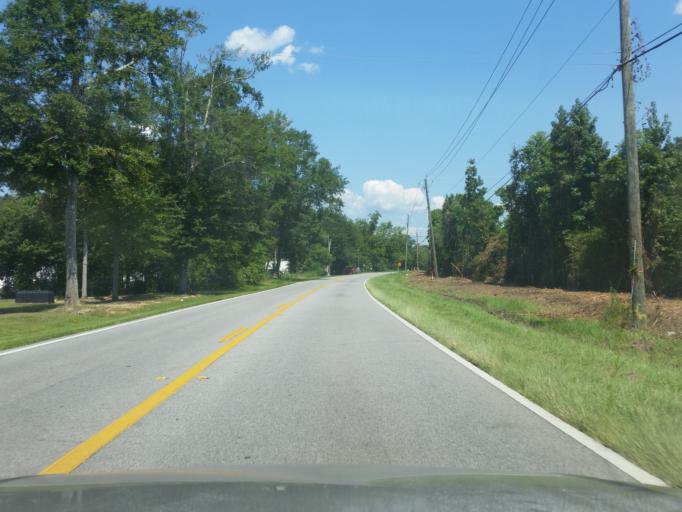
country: US
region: Florida
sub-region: Escambia County
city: Gonzalez
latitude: 30.5915
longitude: -87.3066
